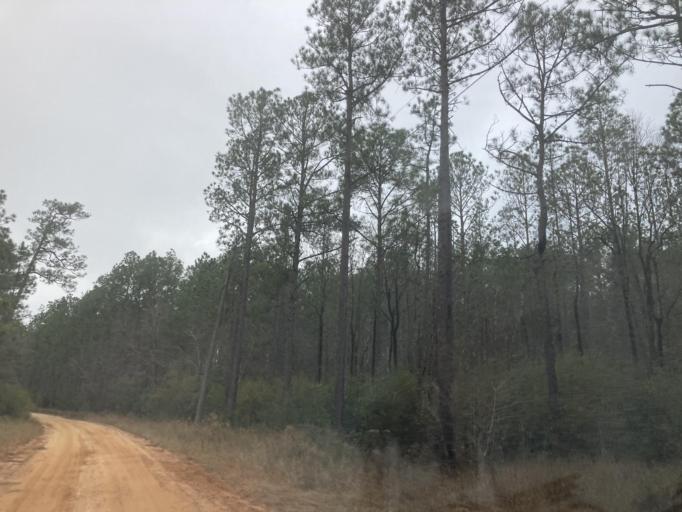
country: US
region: Mississippi
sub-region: Jackson County
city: Latimer
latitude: 30.6829
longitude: -88.9116
